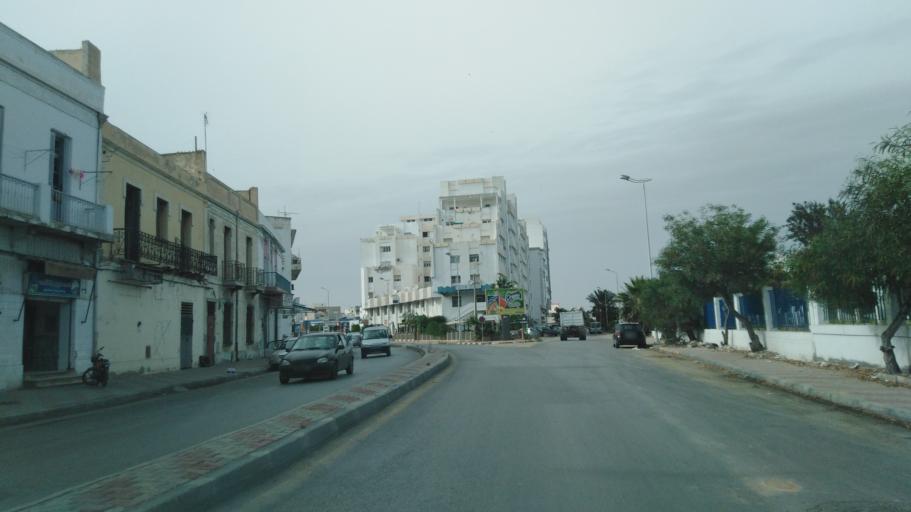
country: TN
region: Safaqis
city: Sfax
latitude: 34.7419
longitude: 10.7640
